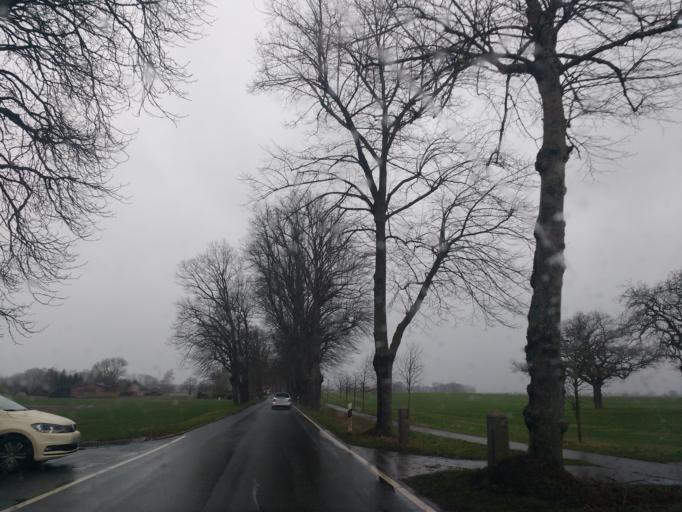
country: DE
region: Schleswig-Holstein
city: Gremersdorf
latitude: 54.3147
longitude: 10.9529
